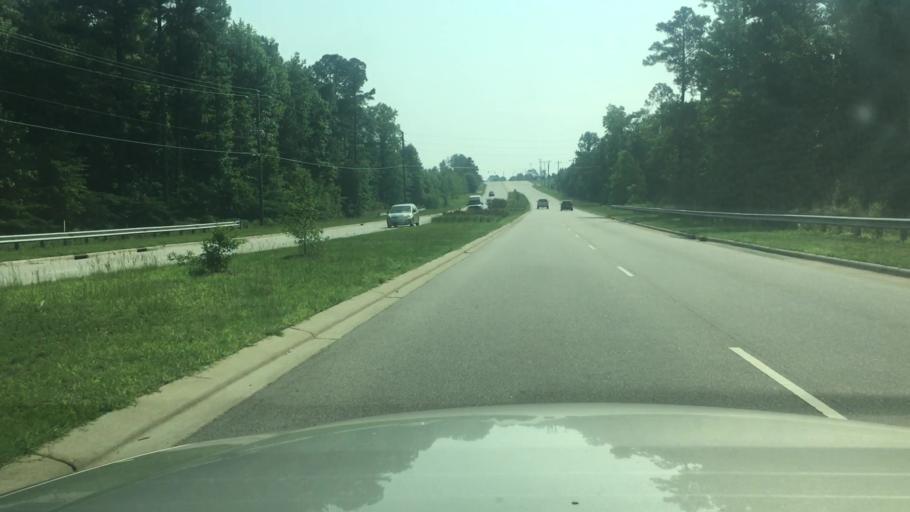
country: US
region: North Carolina
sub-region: Cumberland County
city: Hope Mills
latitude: 34.9884
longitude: -78.9547
